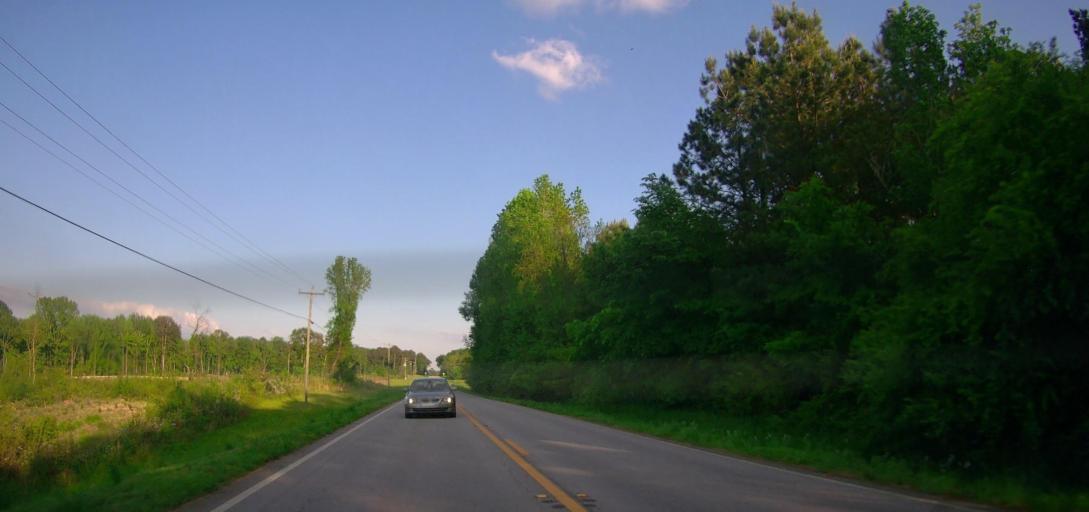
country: US
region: Georgia
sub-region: Jasper County
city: Monticello
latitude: 33.3787
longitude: -83.5464
